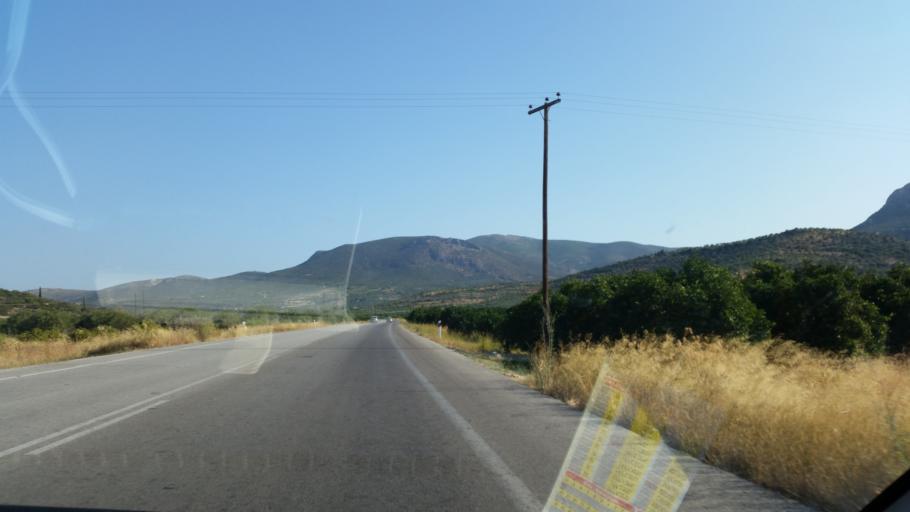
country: GR
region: Peloponnese
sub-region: Nomos Argolidos
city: Koutsopodi
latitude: 37.7293
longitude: 22.7362
